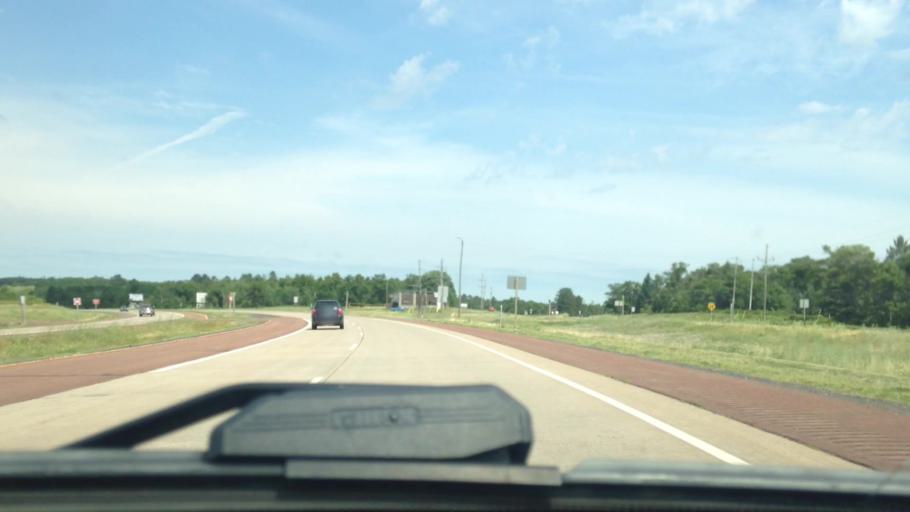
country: US
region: Wisconsin
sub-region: Douglas County
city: Lake Nebagamon
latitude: 46.3187
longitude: -91.8121
